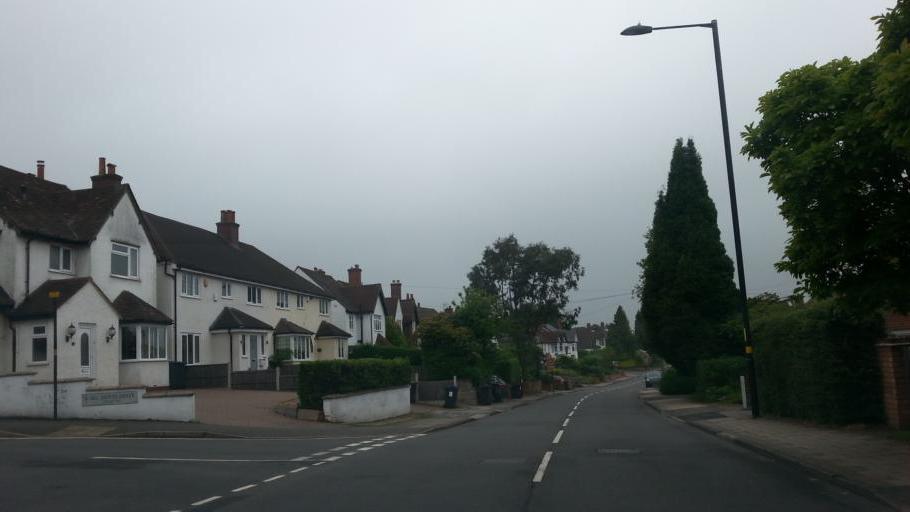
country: GB
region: England
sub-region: City and Borough of Birmingham
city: Sutton Coldfield
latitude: 52.5878
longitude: -1.8378
